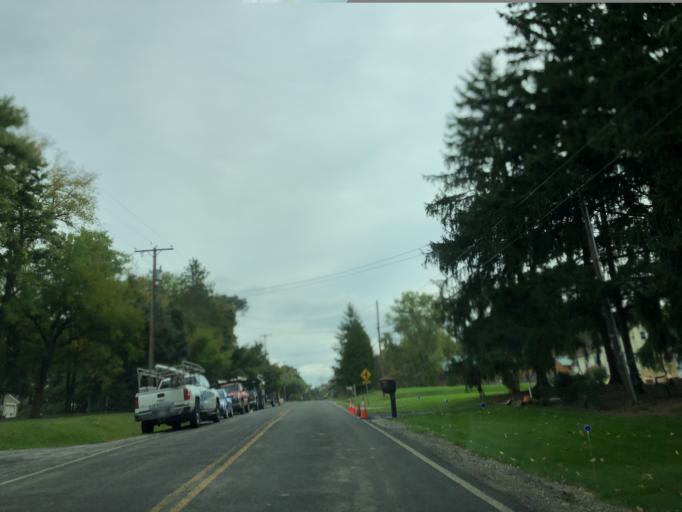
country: US
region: Ohio
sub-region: Summit County
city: Boston Heights
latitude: 41.2905
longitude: -81.5507
